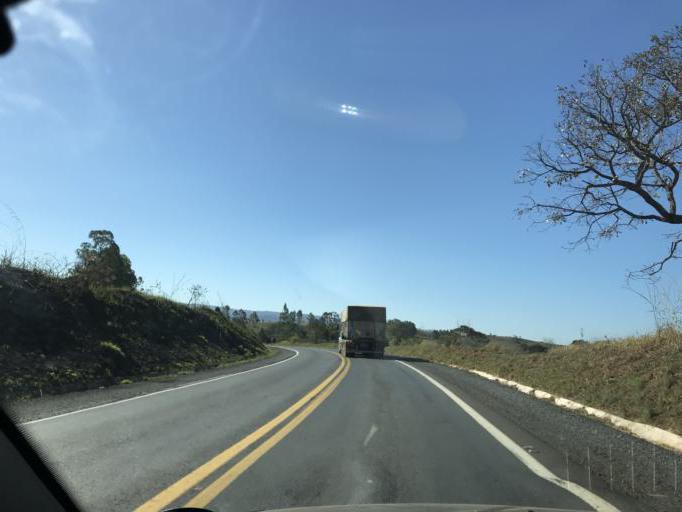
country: BR
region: Minas Gerais
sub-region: Bambui
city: Bambui
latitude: -19.8672
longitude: -45.9855
